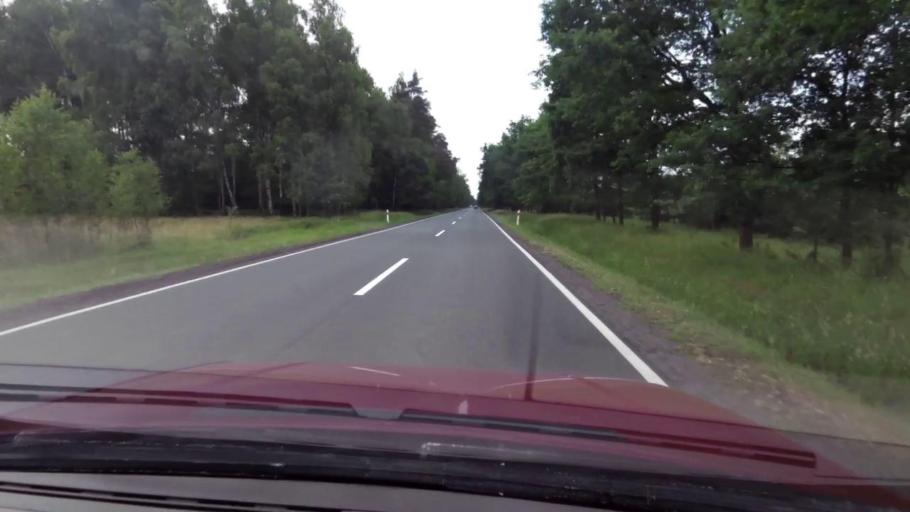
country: PL
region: Pomeranian Voivodeship
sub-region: Powiat bytowski
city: Trzebielino
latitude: 54.2187
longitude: 17.0883
